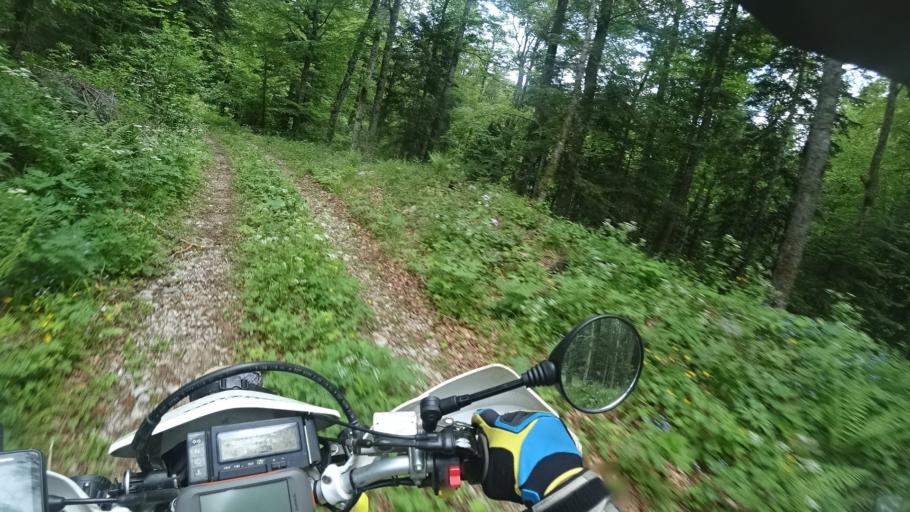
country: HR
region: Zadarska
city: Gracac
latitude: 44.4787
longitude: 15.8923
